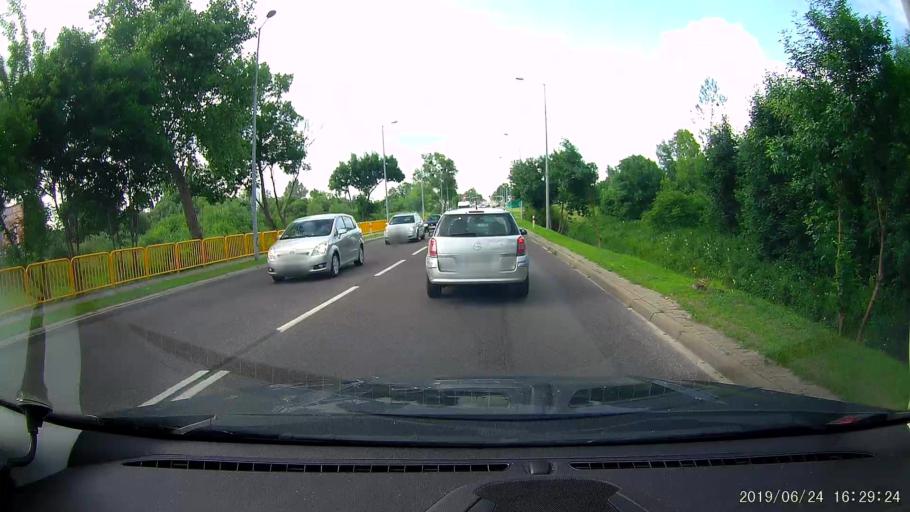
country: PL
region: Lublin Voivodeship
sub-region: Powiat tomaszowski
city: Tomaszow Lubelski
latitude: 50.4589
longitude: 23.4208
